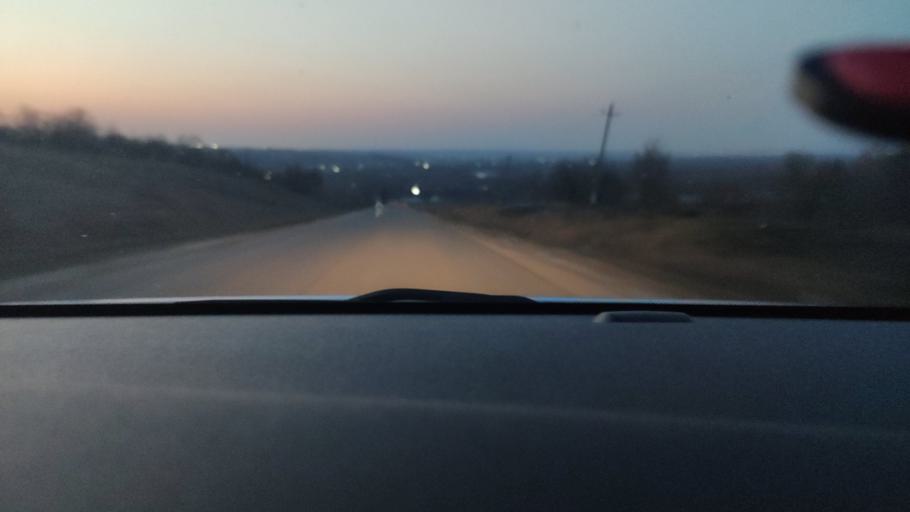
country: RU
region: Voronezj
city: Shilovo
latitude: 51.4550
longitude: 39.0249
